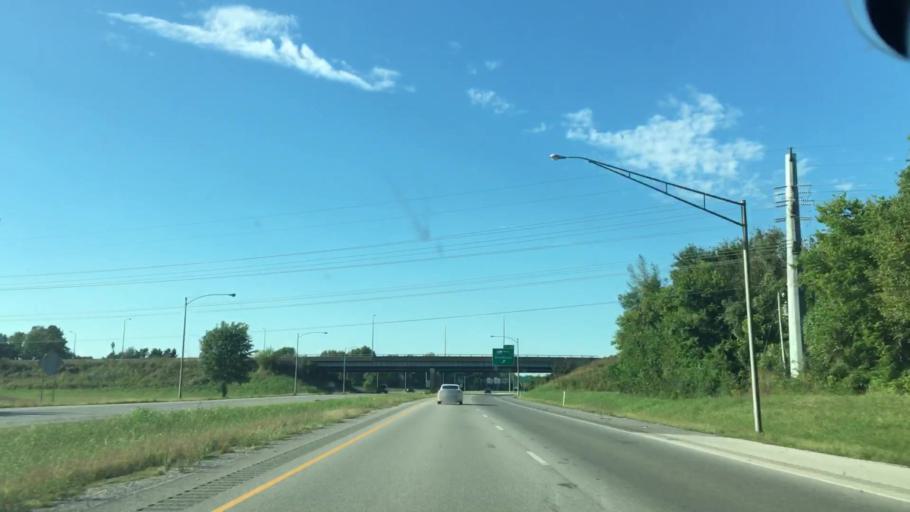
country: US
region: Kentucky
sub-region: Daviess County
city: Owensboro
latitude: 37.7641
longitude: -87.1628
